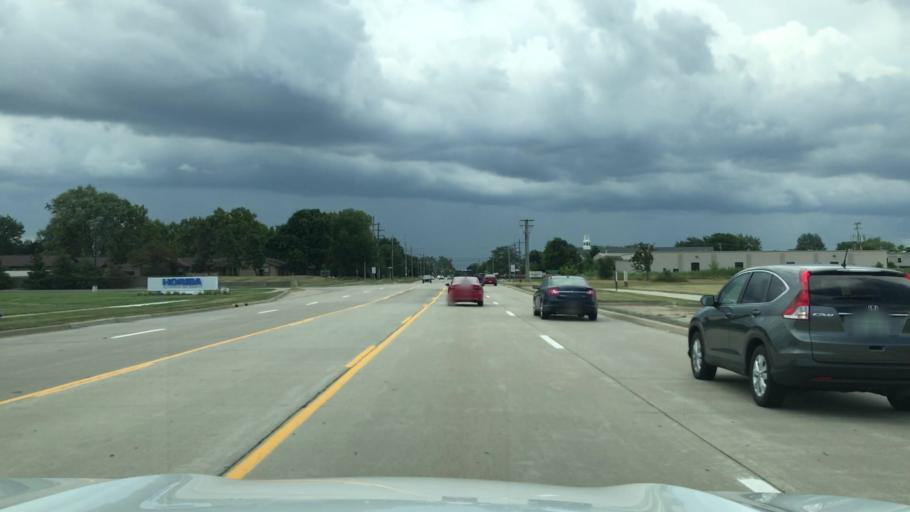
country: US
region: Michigan
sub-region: Oakland County
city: Clawson
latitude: 42.5618
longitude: -83.1082
